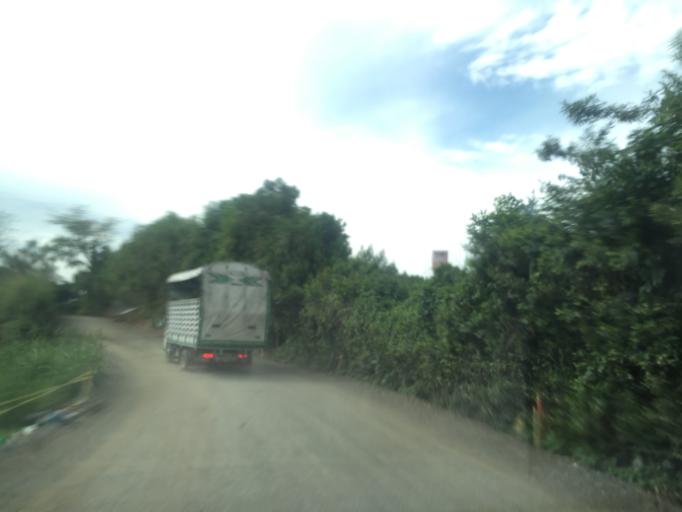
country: CO
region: Quindio
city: La Tebaida
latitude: 4.4582
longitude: -75.7928
